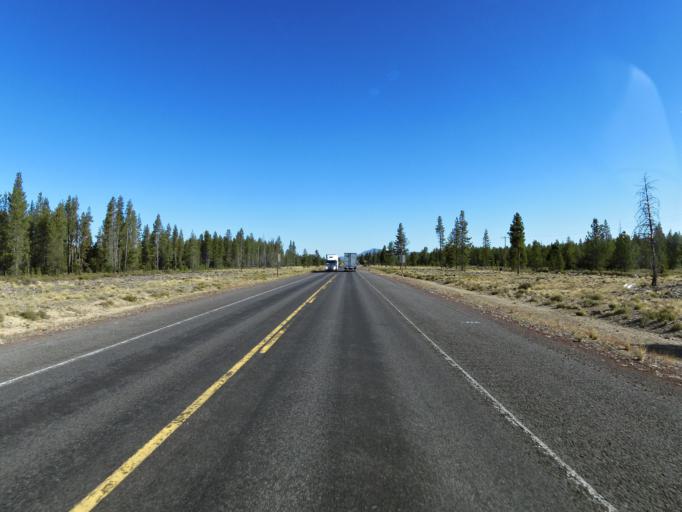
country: US
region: Oregon
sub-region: Deschutes County
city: La Pine
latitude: 43.1260
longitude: -121.8064
